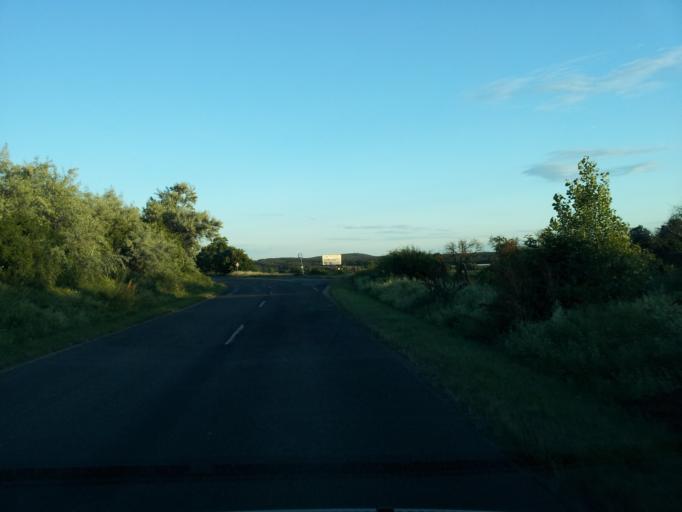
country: HU
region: Veszprem
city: Szentkiralyszabadja
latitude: 47.0393
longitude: 17.9308
